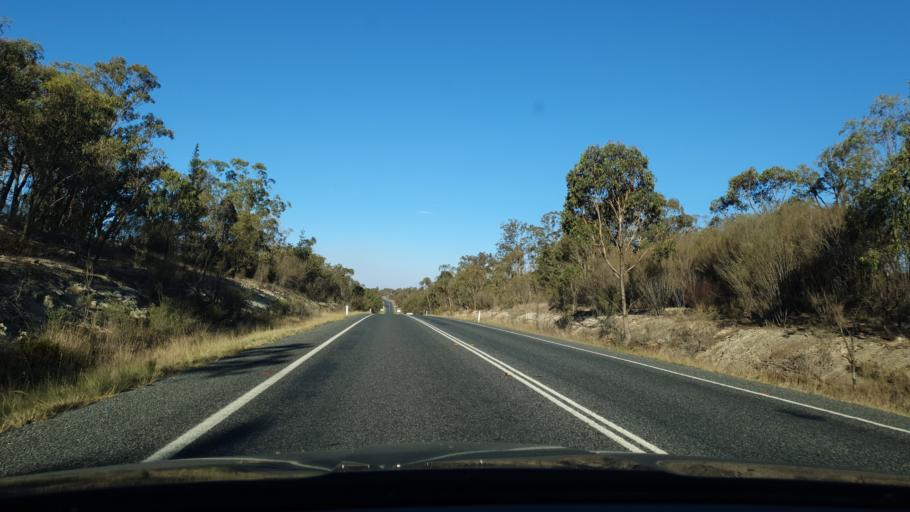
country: AU
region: Queensland
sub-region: Southern Downs
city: Stanthorpe
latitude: -28.6416
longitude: 151.9380
